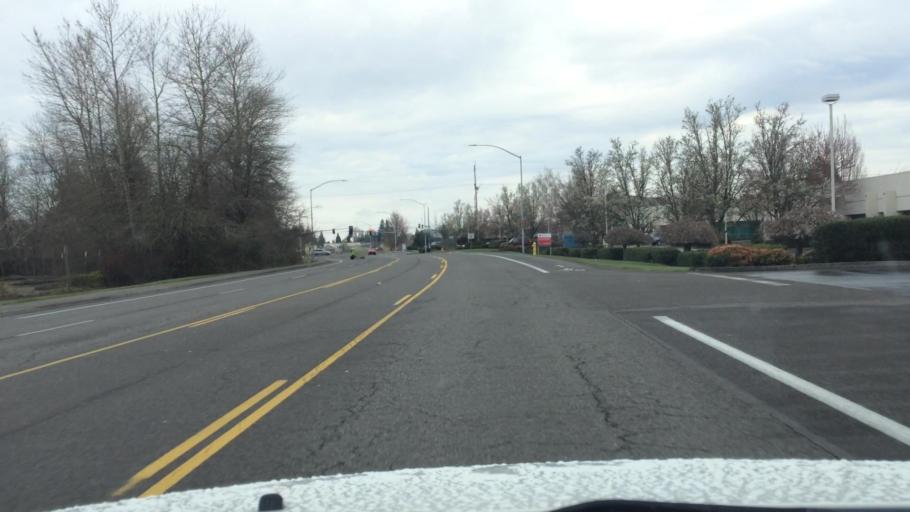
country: US
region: Oregon
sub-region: Marion County
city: Four Corners
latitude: 44.9258
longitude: -122.9938
